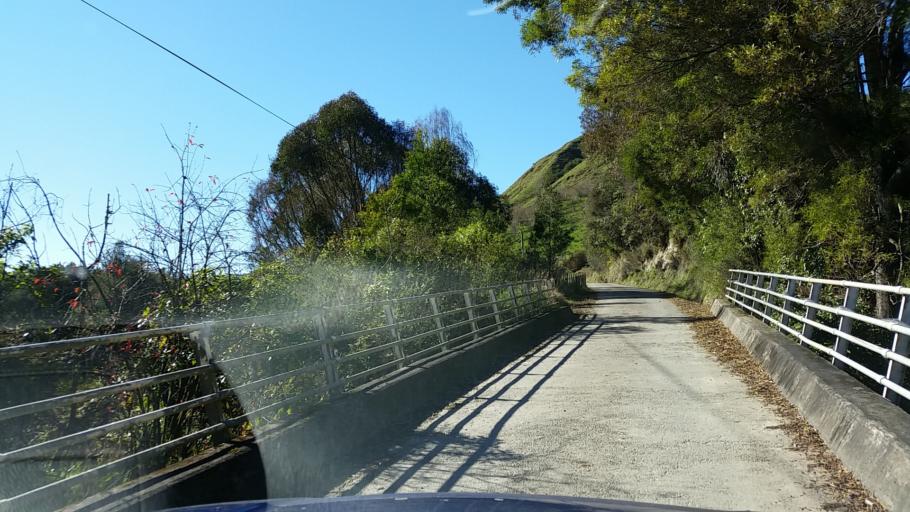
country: NZ
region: Manawatu-Wanganui
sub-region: Wanganui District
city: Wanganui
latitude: -39.5430
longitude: 174.9045
